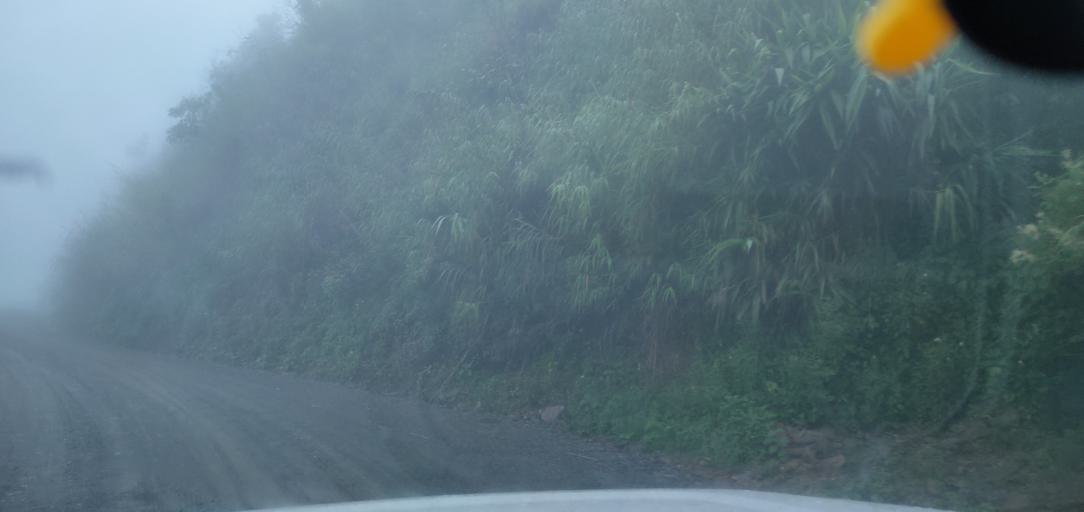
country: LA
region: Phongsali
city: Phongsali
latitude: 21.3968
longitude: 102.2191
